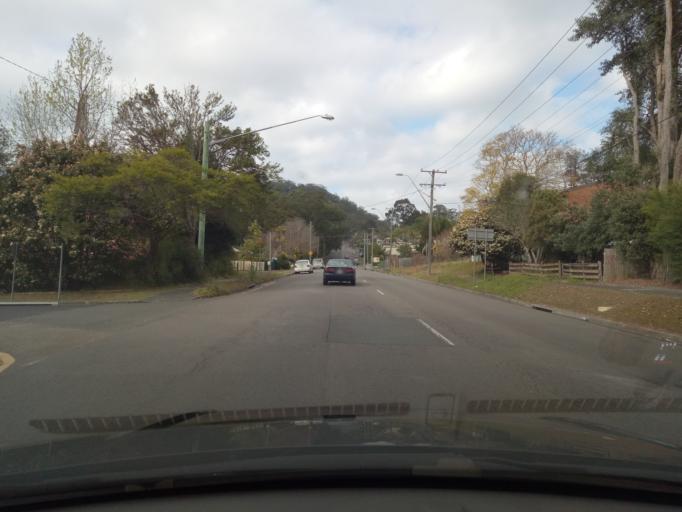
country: AU
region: New South Wales
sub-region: Gosford Shire
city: Gosford
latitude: -33.4145
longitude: 151.3493
